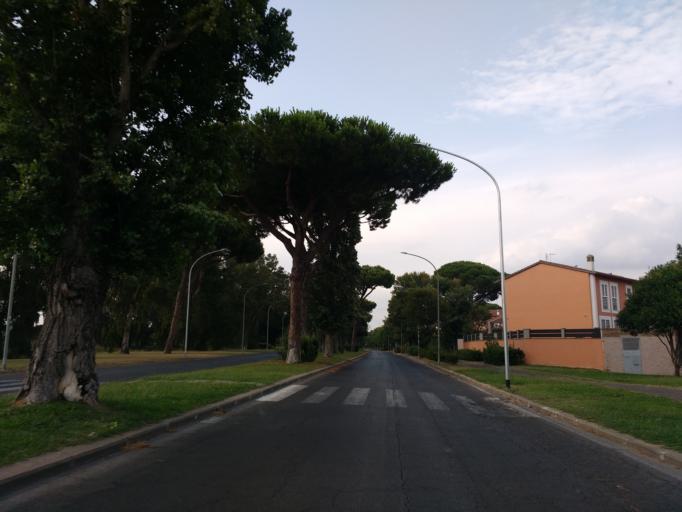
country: IT
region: Latium
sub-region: Citta metropolitana di Roma Capitale
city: Acilia-Castel Fusano-Ostia Antica
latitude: 41.7534
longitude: 12.3504
